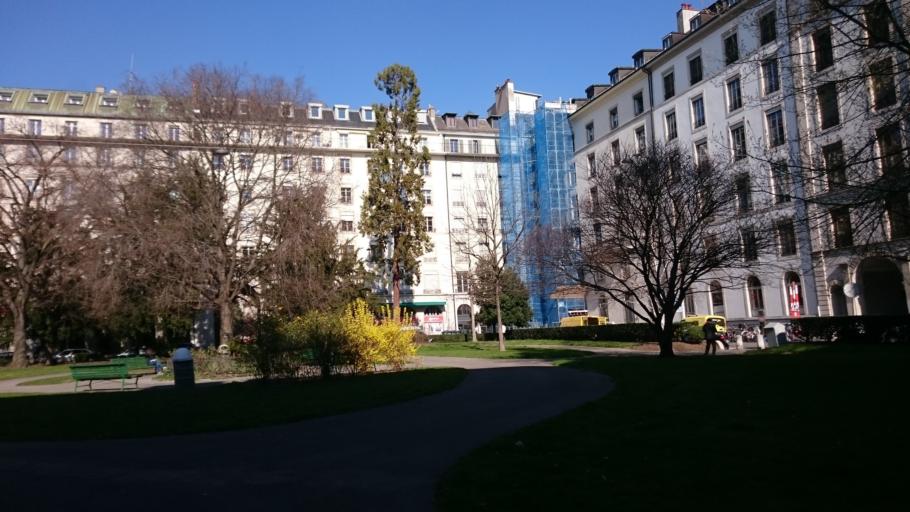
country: CH
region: Geneva
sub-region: Geneva
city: Geneve
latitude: 46.2076
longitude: 6.1474
